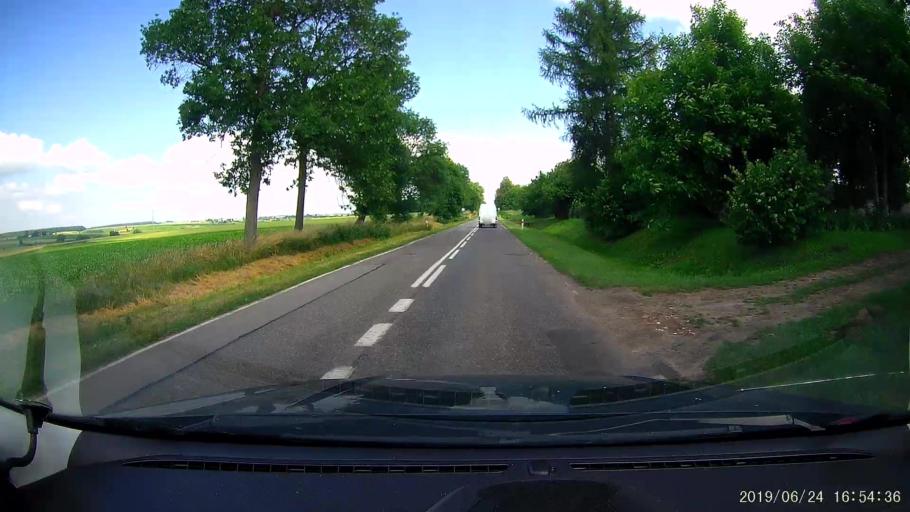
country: PL
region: Lublin Voivodeship
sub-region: Powiat tomaszowski
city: Telatyn
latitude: 50.5312
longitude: 23.8167
